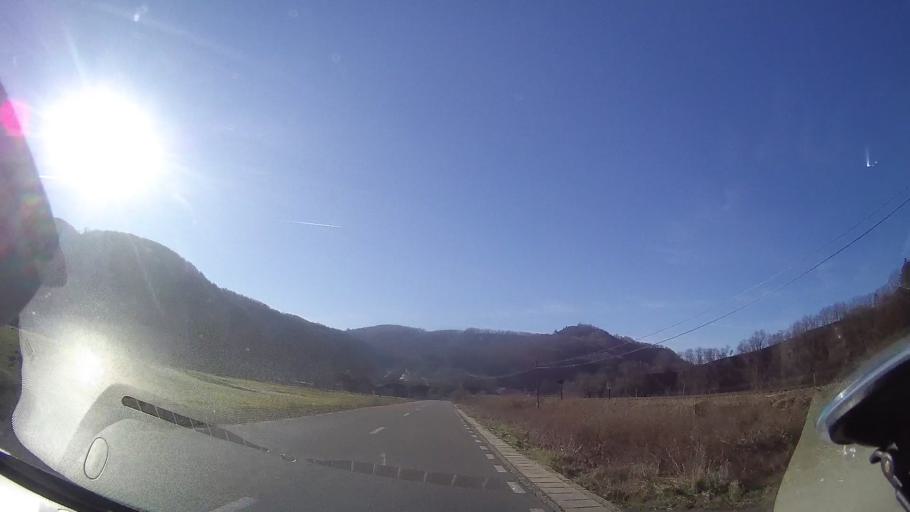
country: RO
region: Bihor
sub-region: Comuna Bratca
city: Bratca
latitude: 46.9221
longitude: 22.6249
